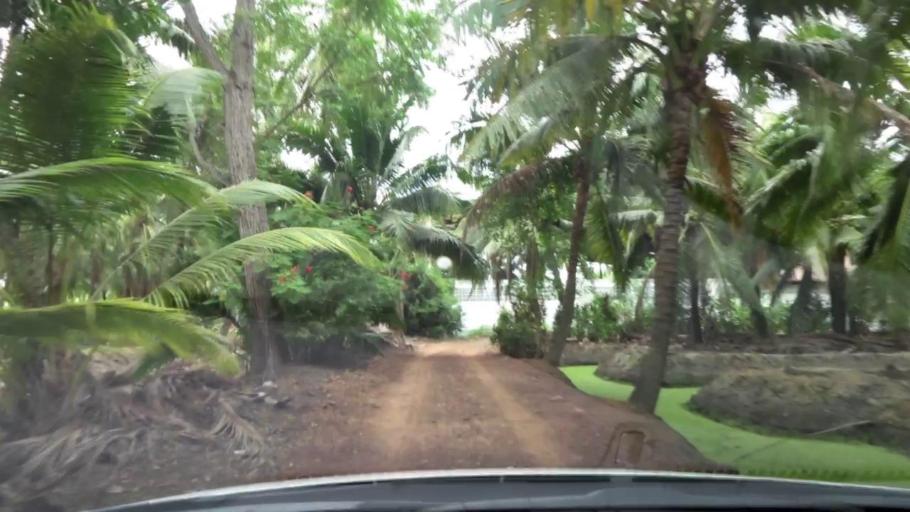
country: TH
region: Ratchaburi
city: Damnoen Saduak
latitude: 13.5765
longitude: 99.9789
